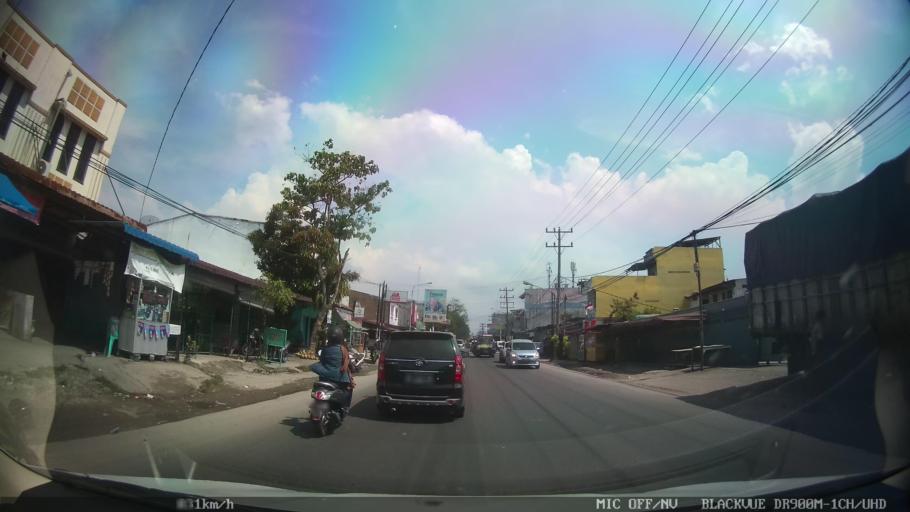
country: ID
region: North Sumatra
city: Medan
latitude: 3.6314
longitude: 98.6611
